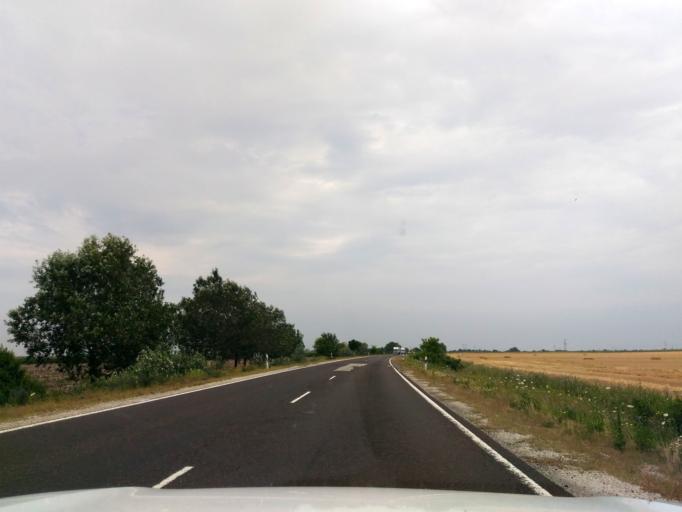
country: HU
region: Pest
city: Abony
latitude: 47.1982
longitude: 20.0796
